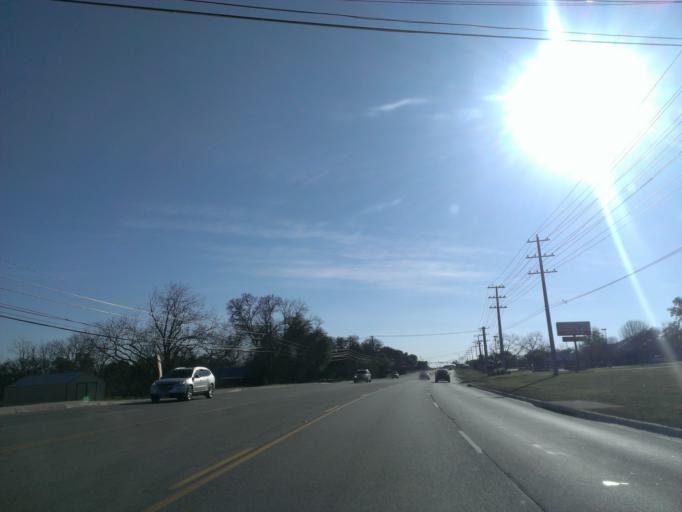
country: US
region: Texas
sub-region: Burnet County
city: Burnet
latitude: 30.7483
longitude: -98.2295
